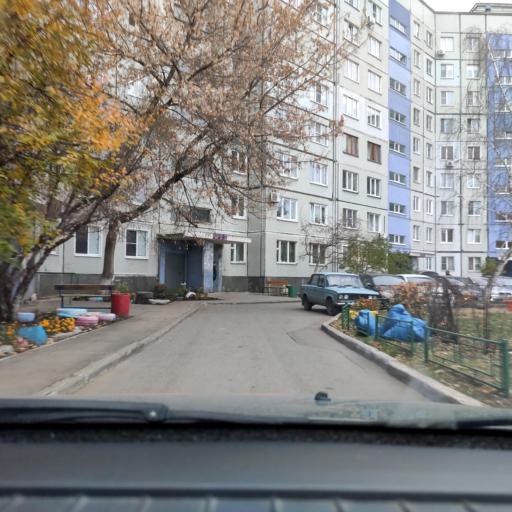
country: RU
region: Samara
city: Tol'yatti
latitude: 53.5404
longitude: 49.4056
